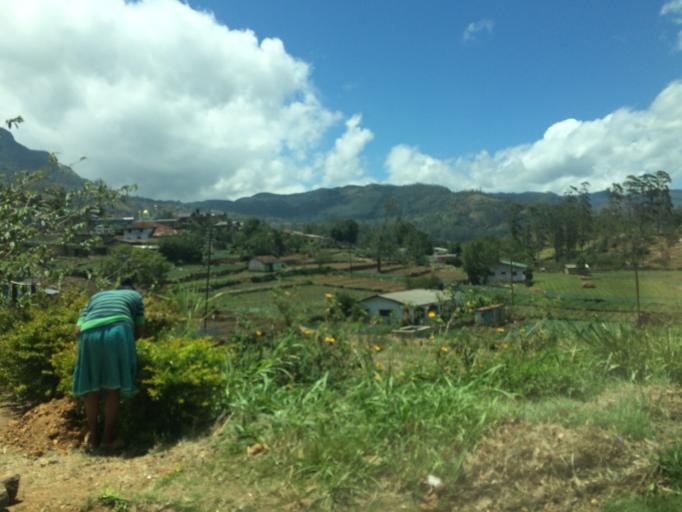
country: LK
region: Central
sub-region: Nuwara Eliya District
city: Nuwara Eliya
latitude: 6.9048
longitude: 80.8460
